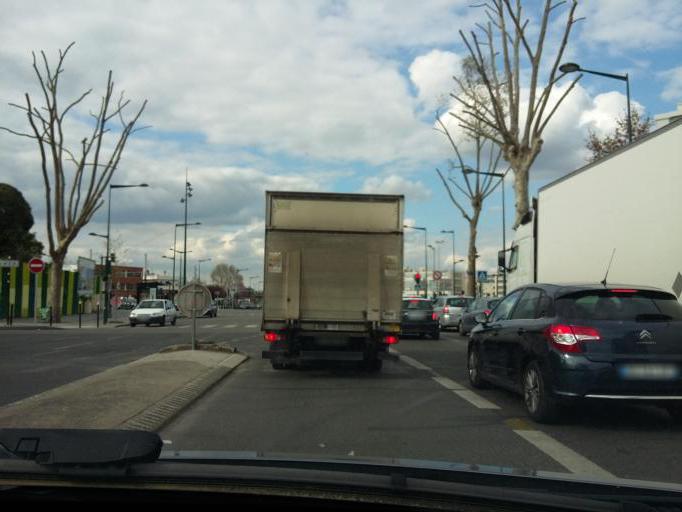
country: FR
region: Ile-de-France
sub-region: Departement de Seine-Saint-Denis
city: Epinay-sur-Seine
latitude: 48.9539
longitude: 2.3077
